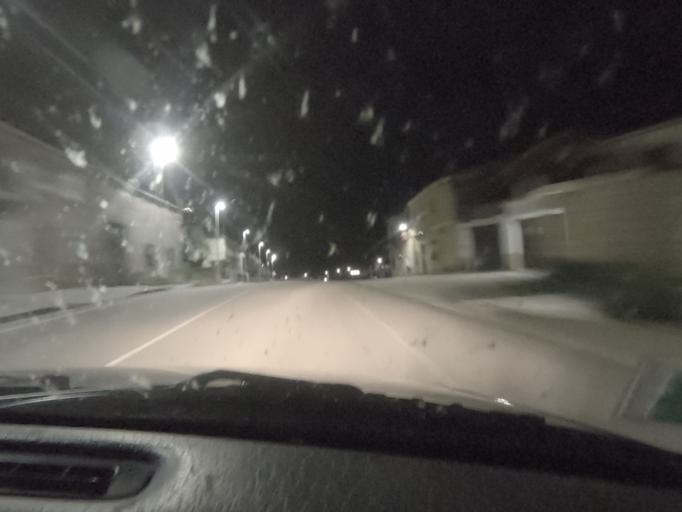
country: ES
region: Castille and Leon
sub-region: Provincia de Salamanca
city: Robleda
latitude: 40.3870
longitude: -6.6081
